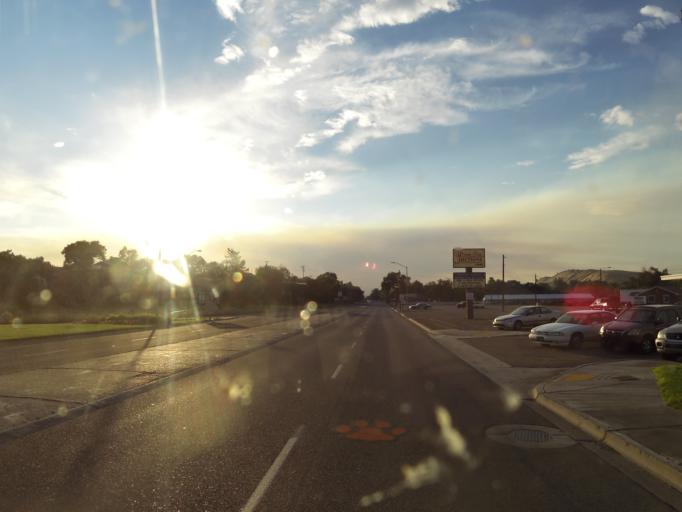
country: US
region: Idaho
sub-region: Bannock County
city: Pocatello
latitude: 42.8417
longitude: -112.4134
